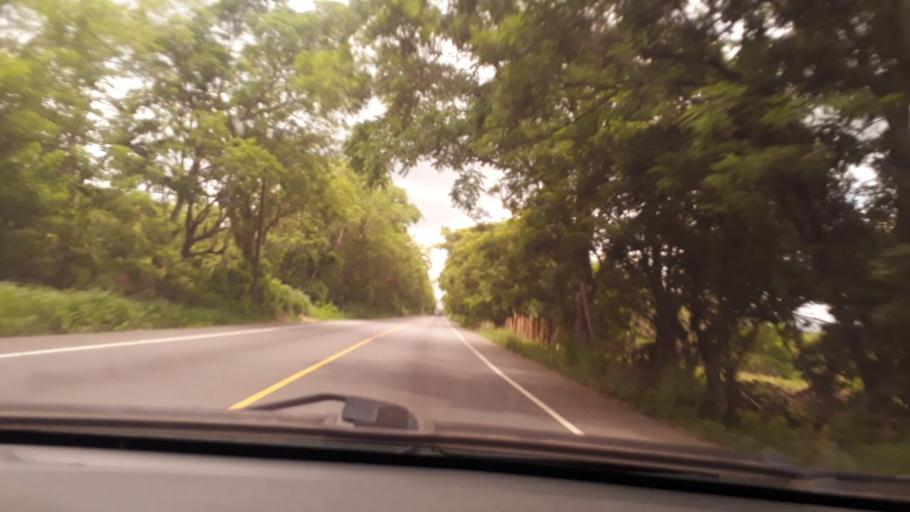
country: GT
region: Izabal
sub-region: Municipio de Los Amates
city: Los Amates
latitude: 15.2187
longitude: -89.2252
